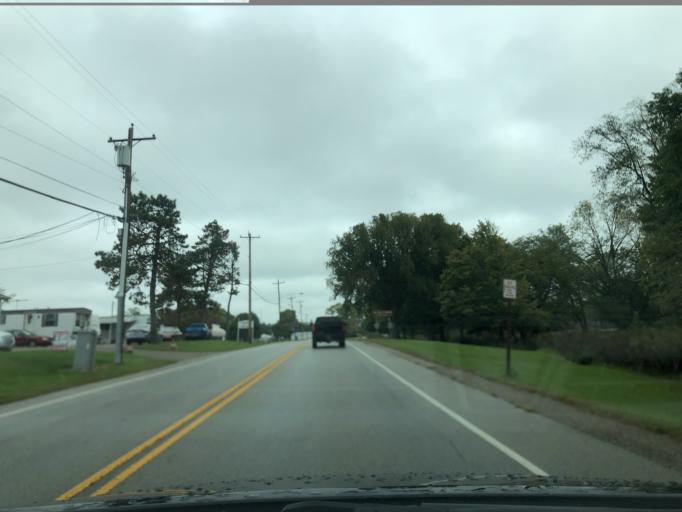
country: US
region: Ohio
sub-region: Hamilton County
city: Sharonville
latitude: 39.2756
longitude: -84.4103
